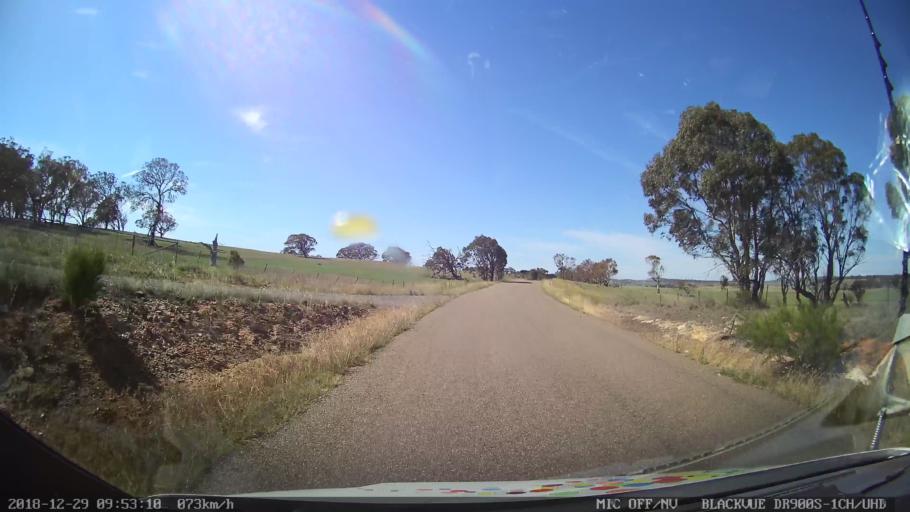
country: AU
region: New South Wales
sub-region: Goulburn Mulwaree
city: Goulburn
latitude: -34.7486
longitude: 149.4699
